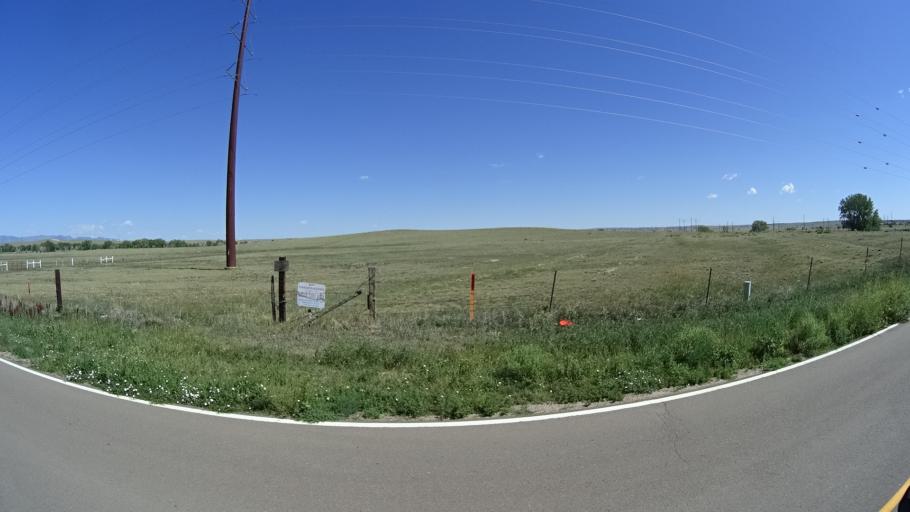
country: US
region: Colorado
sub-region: El Paso County
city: Security-Widefield
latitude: 38.7810
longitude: -104.6405
